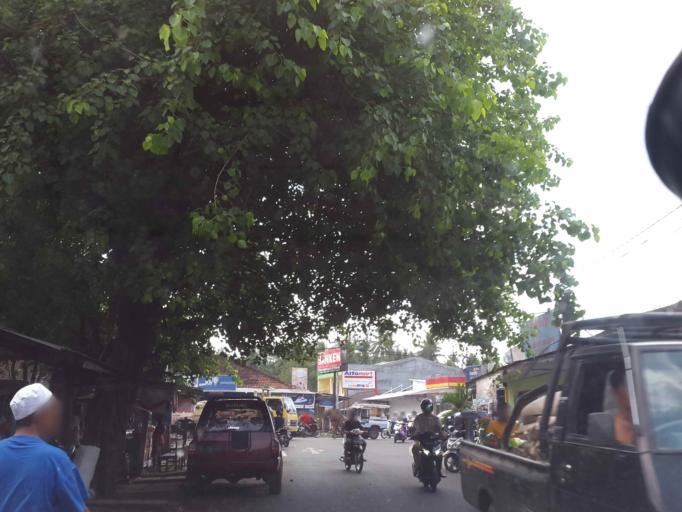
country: ID
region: West Nusa Tenggara
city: Mambalan
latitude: -8.5432
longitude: 116.1067
